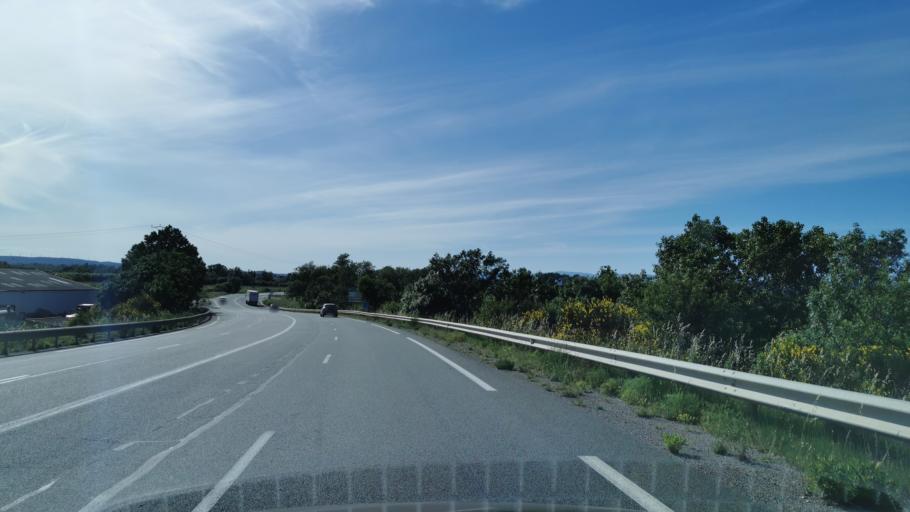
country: FR
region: Languedoc-Roussillon
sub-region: Departement de l'Aude
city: Canet
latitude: 43.2119
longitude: 2.8730
